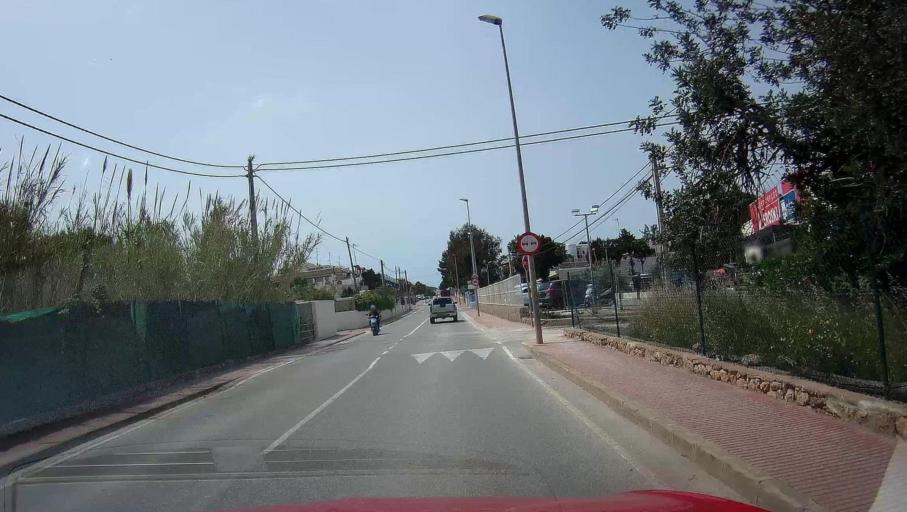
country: ES
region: Balearic Islands
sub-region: Illes Balears
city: Santa Eularia des Riu
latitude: 38.9922
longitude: 1.5478
